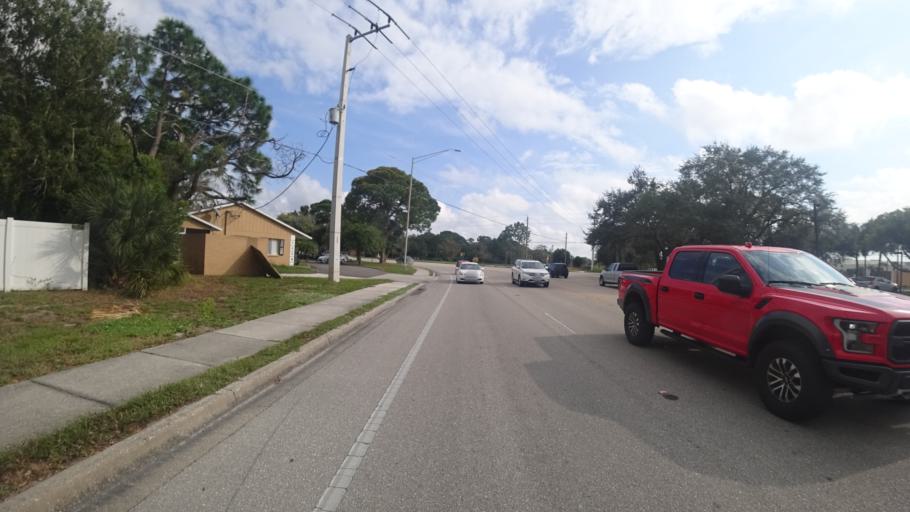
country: US
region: Florida
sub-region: Manatee County
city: Bayshore Gardens
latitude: 27.4300
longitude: -82.5735
